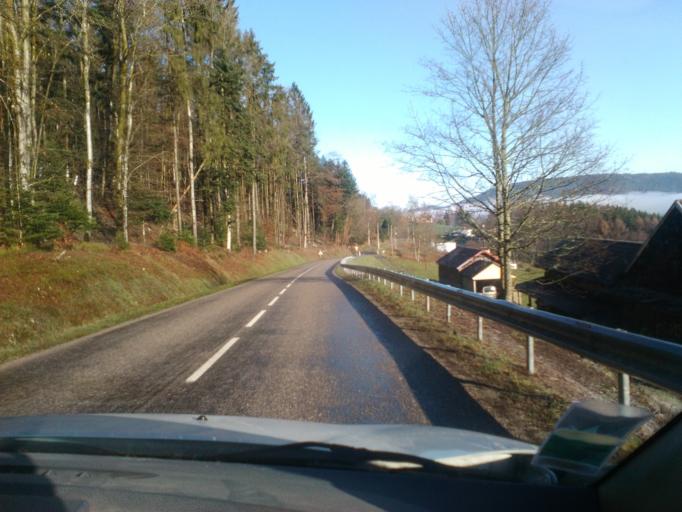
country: FR
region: Lorraine
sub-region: Departement des Vosges
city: Remiremont
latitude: 47.9982
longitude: 6.5733
